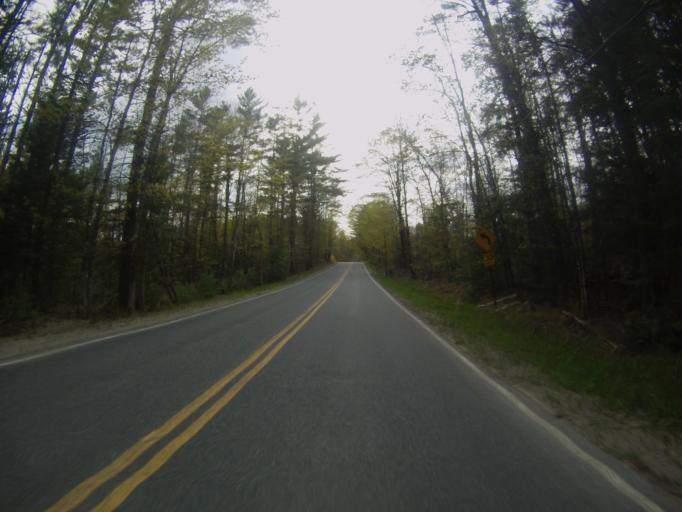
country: US
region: New York
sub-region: Warren County
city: Warrensburg
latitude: 43.8424
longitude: -73.8684
